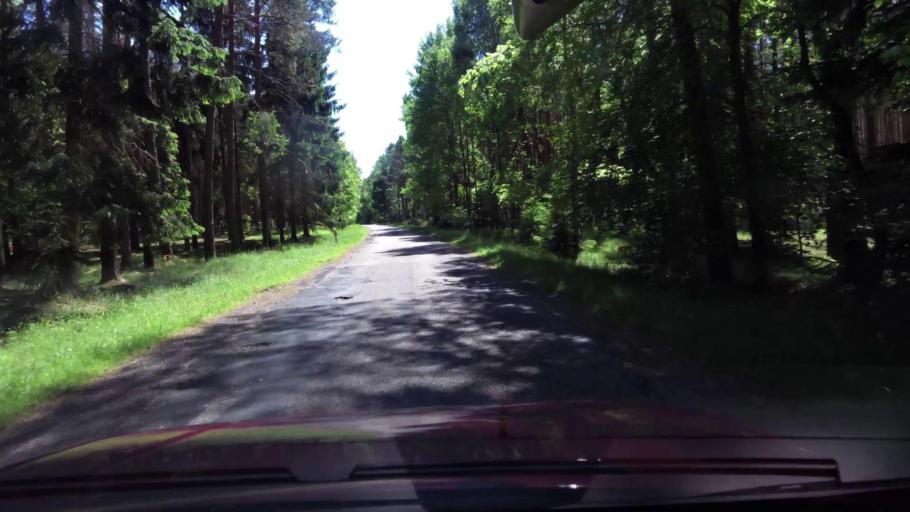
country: PL
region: West Pomeranian Voivodeship
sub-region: Powiat koszalinski
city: Bobolice
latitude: 54.0541
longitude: 16.5791
